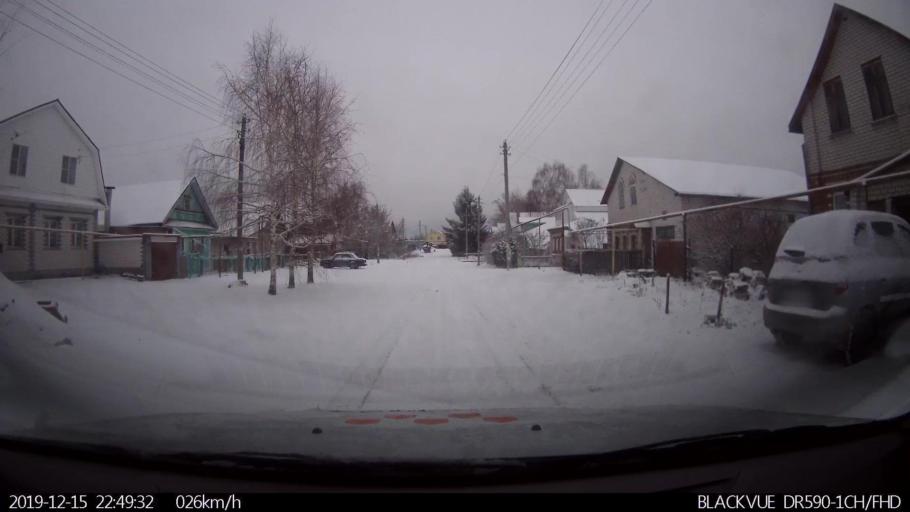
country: RU
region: Nizjnij Novgorod
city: Afonino
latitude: 56.2195
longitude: 44.1136
